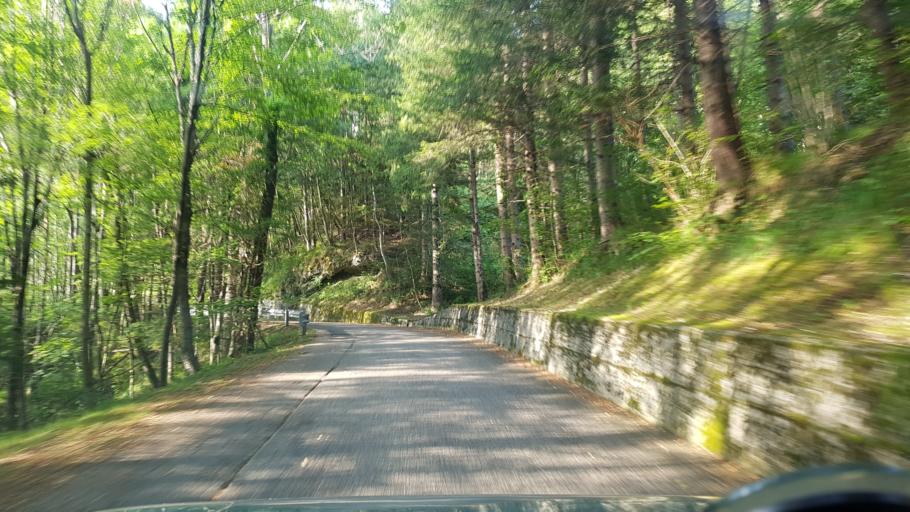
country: IT
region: Friuli Venezia Giulia
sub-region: Provincia di Udine
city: Lusevera
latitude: 46.3089
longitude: 13.2739
